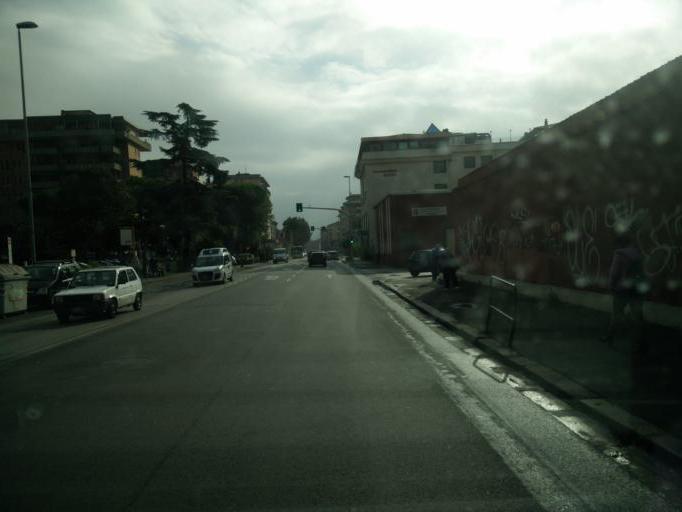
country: IT
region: Tuscany
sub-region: Province of Florence
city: Sesto Fiorentino
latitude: 43.7943
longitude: 11.2095
